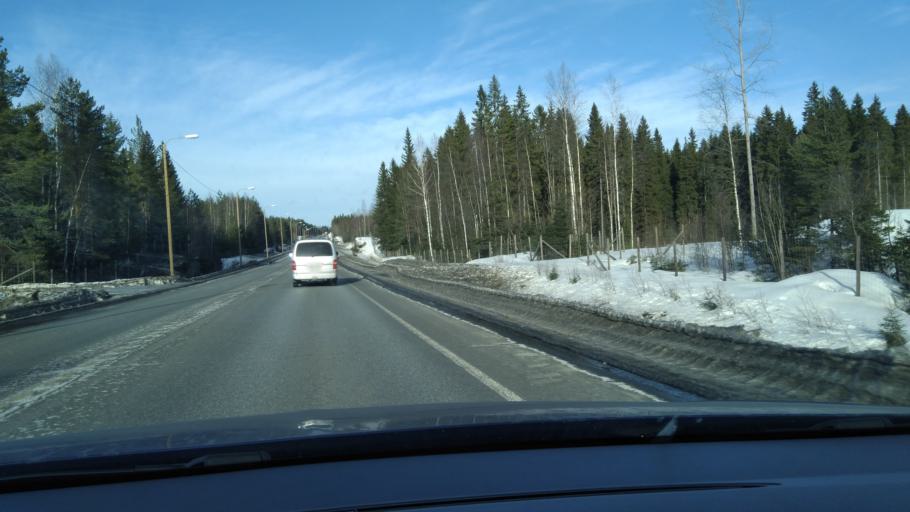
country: FI
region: Pirkanmaa
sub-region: Tampere
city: Orivesi
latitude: 61.6603
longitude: 24.2583
